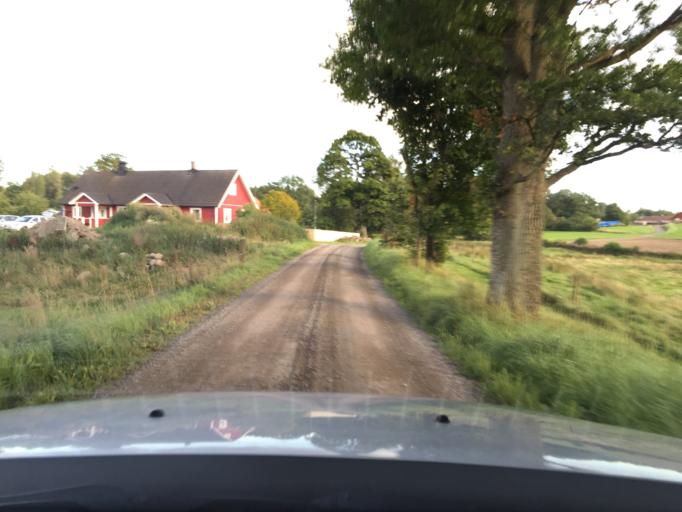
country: SE
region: Skane
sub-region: Hassleholms Kommun
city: Sosdala
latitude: 56.0409
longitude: 13.7096
